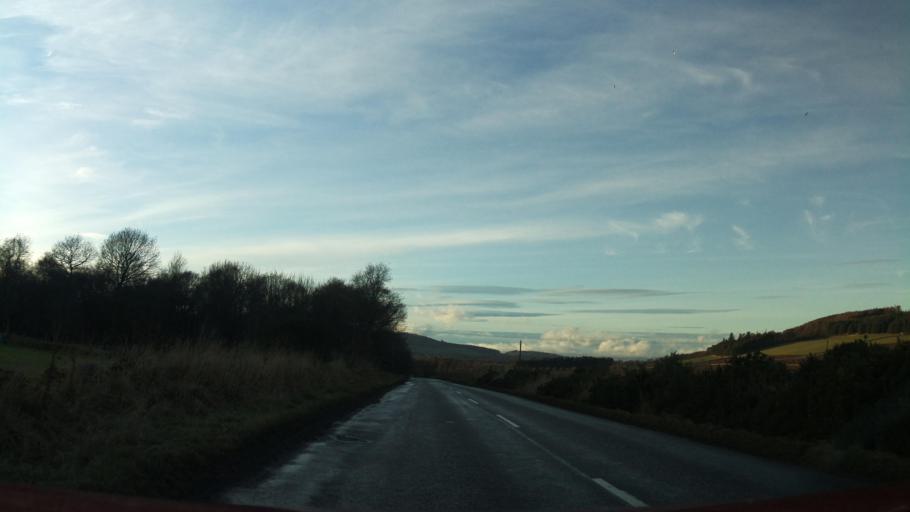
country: GB
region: Scotland
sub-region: Angus
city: Forfar
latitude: 56.5863
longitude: -2.8528
